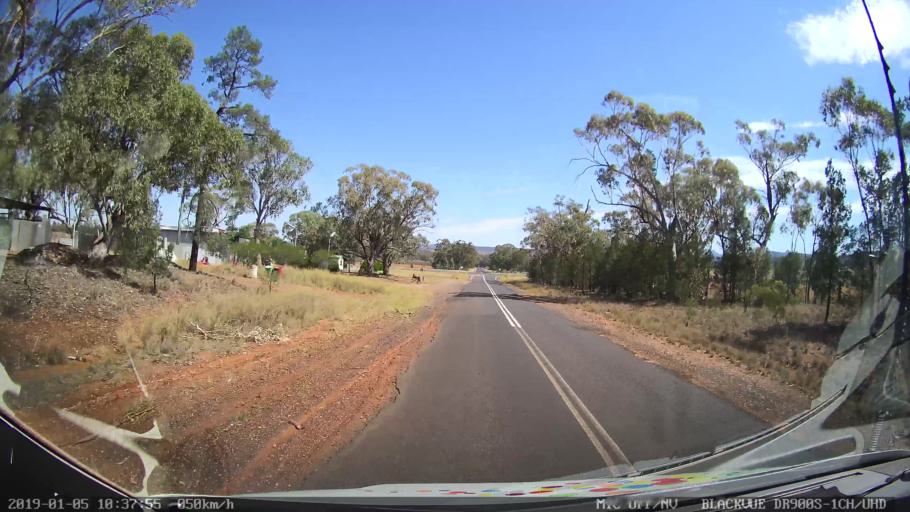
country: AU
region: New South Wales
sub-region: Gilgandra
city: Gilgandra
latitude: -31.4712
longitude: 148.9205
